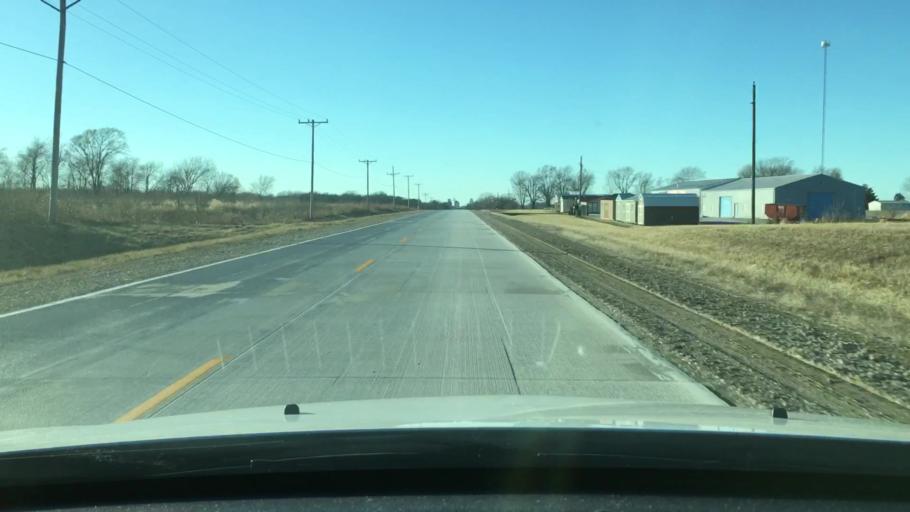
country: US
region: Missouri
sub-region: Boone County
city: Centralia
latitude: 39.2058
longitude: -92.0915
